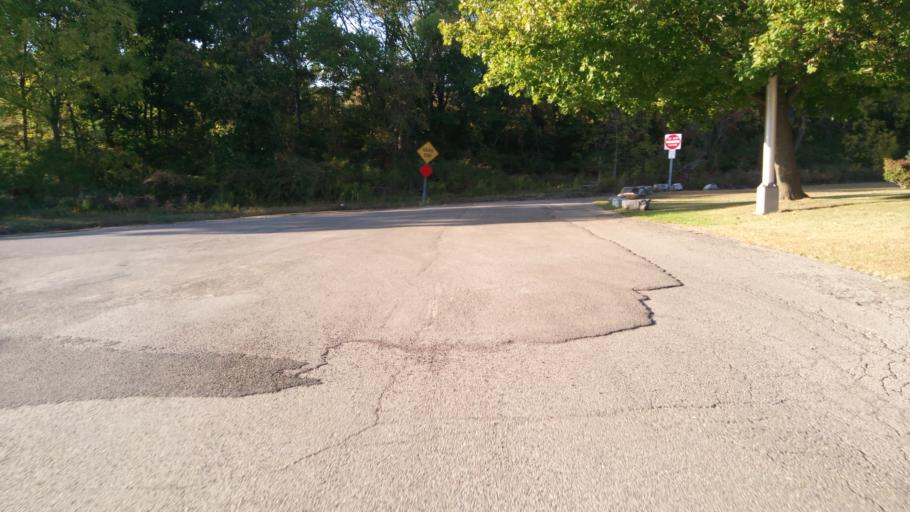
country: US
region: New York
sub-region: Chemung County
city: Southport
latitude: 42.0564
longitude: -76.8362
